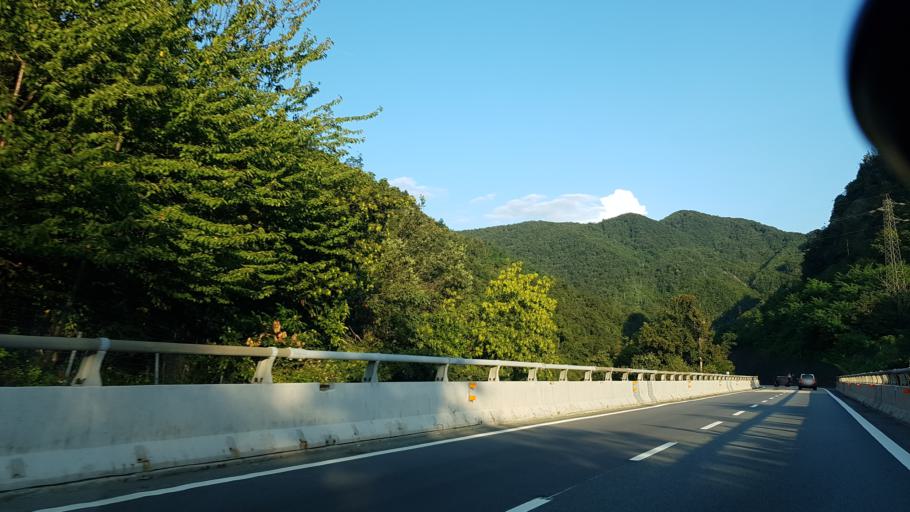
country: IT
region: Piedmont
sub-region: Provincia di Alessandria
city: Arquata Scrivia
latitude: 44.6627
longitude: 8.9141
